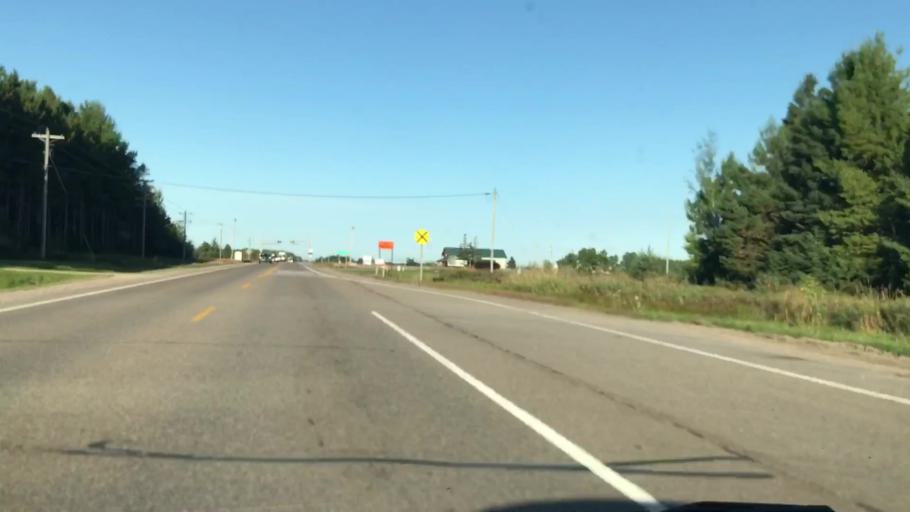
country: US
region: Michigan
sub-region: Chippewa County
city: Sault Ste. Marie
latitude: 46.3745
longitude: -84.4233
